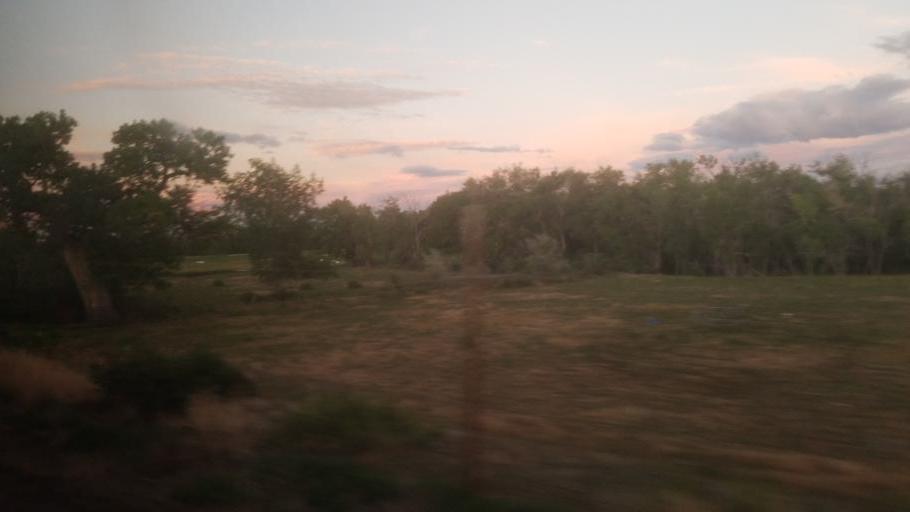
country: US
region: Colorado
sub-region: Las Animas County
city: Trinidad
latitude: 37.2432
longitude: -104.4227
